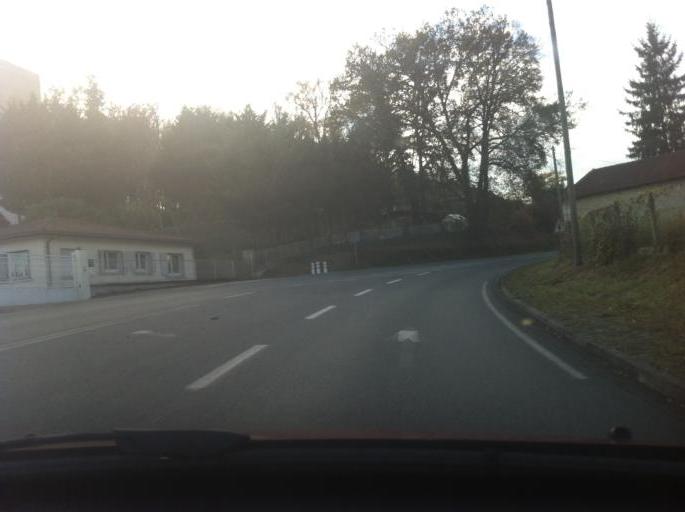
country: FR
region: Aquitaine
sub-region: Departement de la Dordogne
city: Chancelade
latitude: 45.1955
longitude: 0.6394
